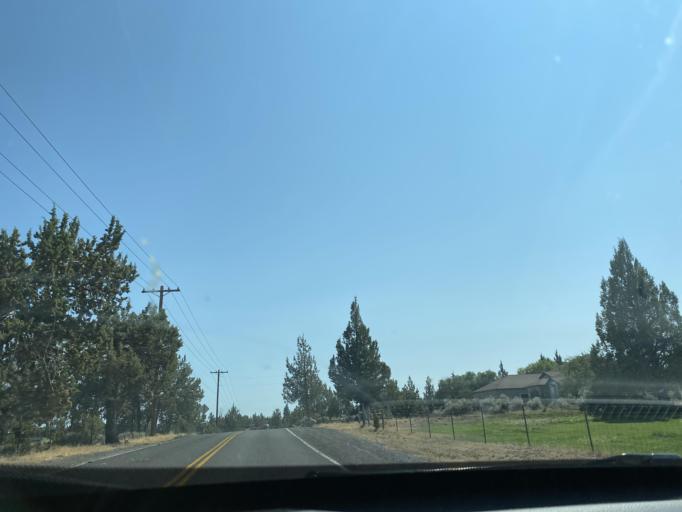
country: US
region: Oregon
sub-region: Deschutes County
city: Terrebonne
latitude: 44.3702
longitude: -121.1635
